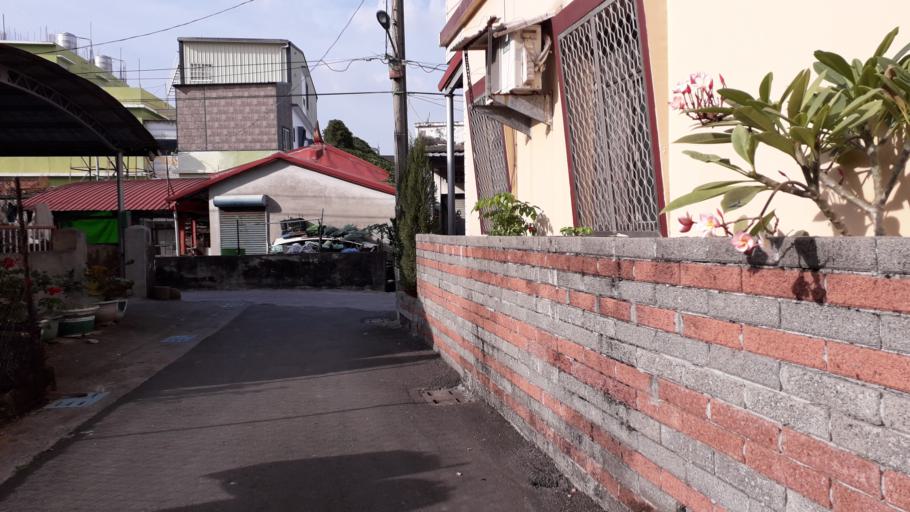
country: TW
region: Taiwan
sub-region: Pingtung
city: Pingtung
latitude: 22.3589
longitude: 120.5988
